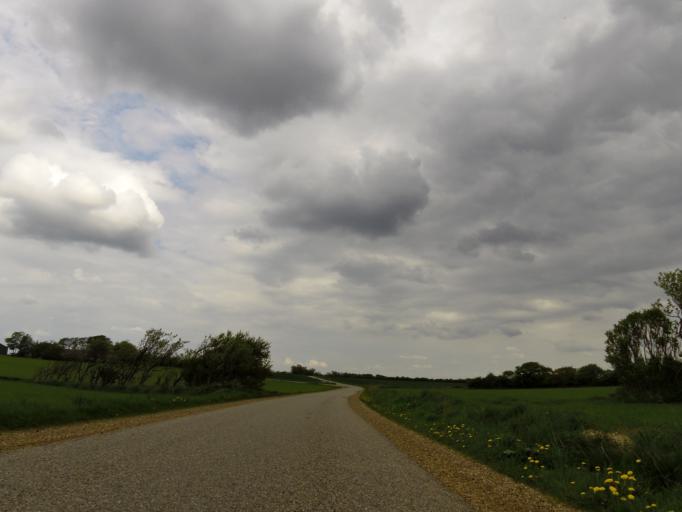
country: DK
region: Central Jutland
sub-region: Holstebro Kommune
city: Vinderup
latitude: 56.5260
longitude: 8.7900
